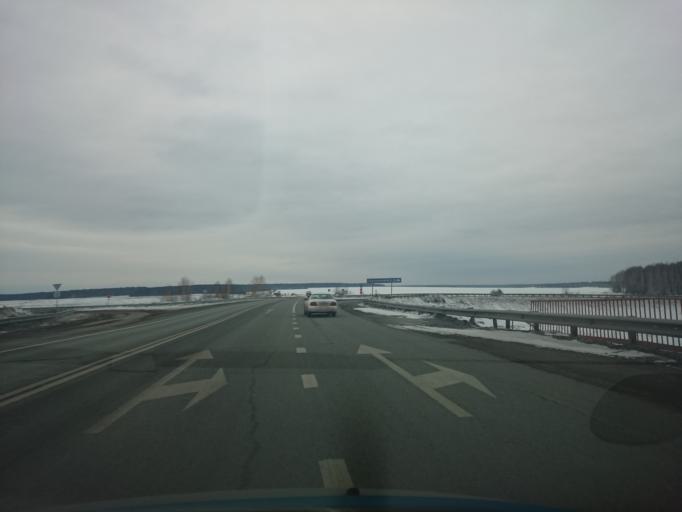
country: RU
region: Sverdlovsk
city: Achit
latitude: 56.7892
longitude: 57.8818
